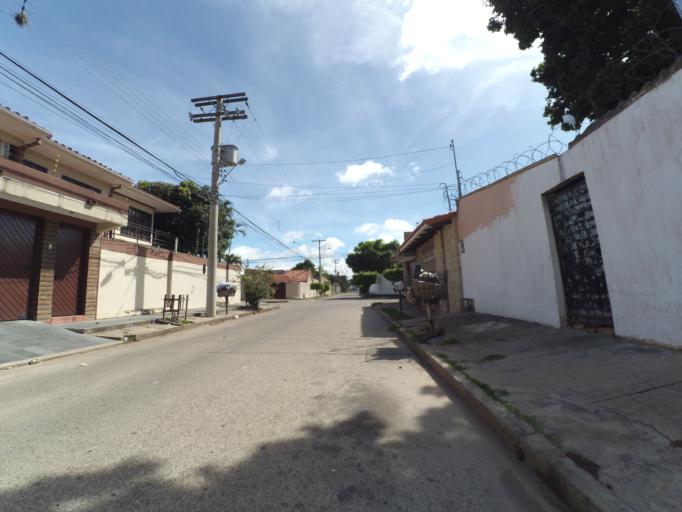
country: BO
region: Santa Cruz
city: Santa Cruz de la Sierra
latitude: -17.7593
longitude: -63.1553
